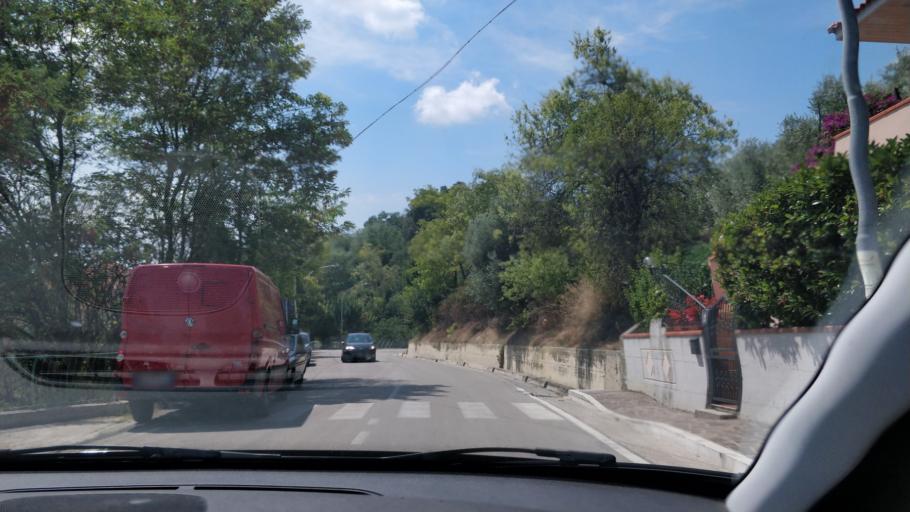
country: IT
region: Abruzzo
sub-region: Provincia di Chieti
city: Sambuceto
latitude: 42.4092
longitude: 14.2012
